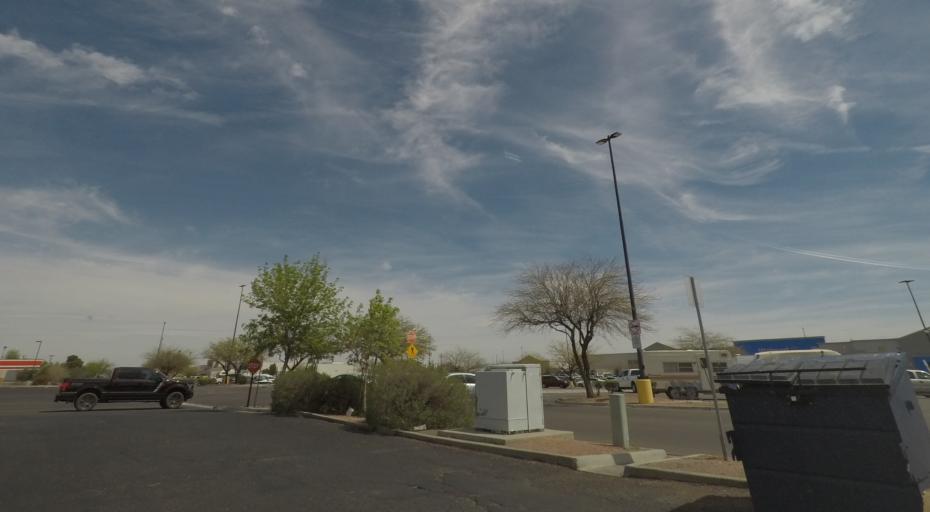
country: US
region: Arizona
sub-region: Mohave County
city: Kingman
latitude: 35.2219
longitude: -114.0353
